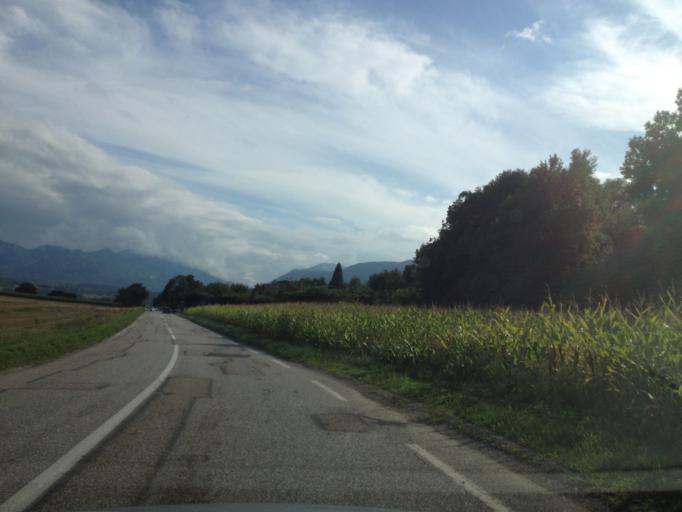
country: FR
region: Rhone-Alpes
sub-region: Departement de la Savoie
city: Le Bourget-du-Lac
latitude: 45.6211
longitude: 5.8613
